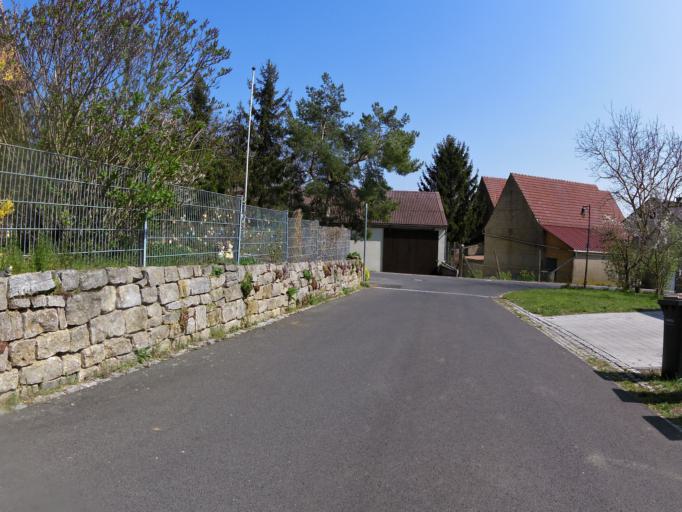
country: DE
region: Bavaria
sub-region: Regierungsbezirk Unterfranken
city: Dettelbach
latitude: 49.8195
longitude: 10.1490
